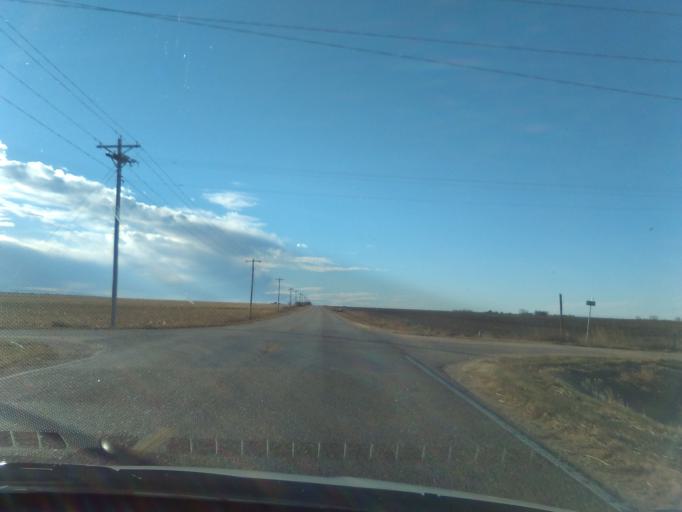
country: US
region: Nebraska
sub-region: Kearney County
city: Minden
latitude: 40.3653
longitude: -99.0842
